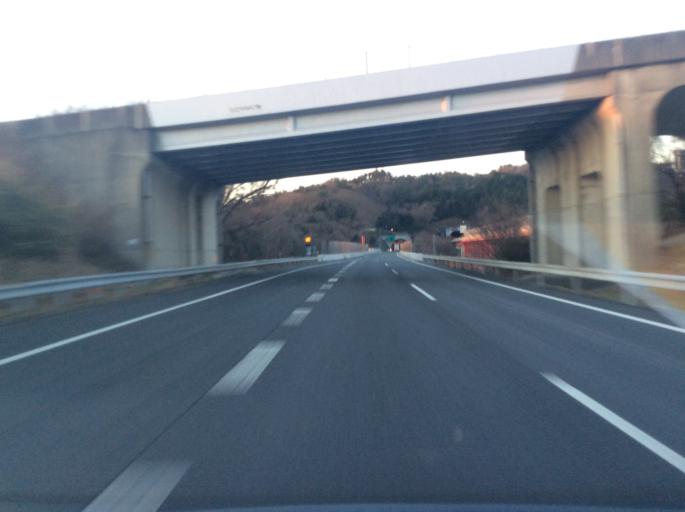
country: JP
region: Ibaraki
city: Hitachi
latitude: 36.6016
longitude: 140.6361
